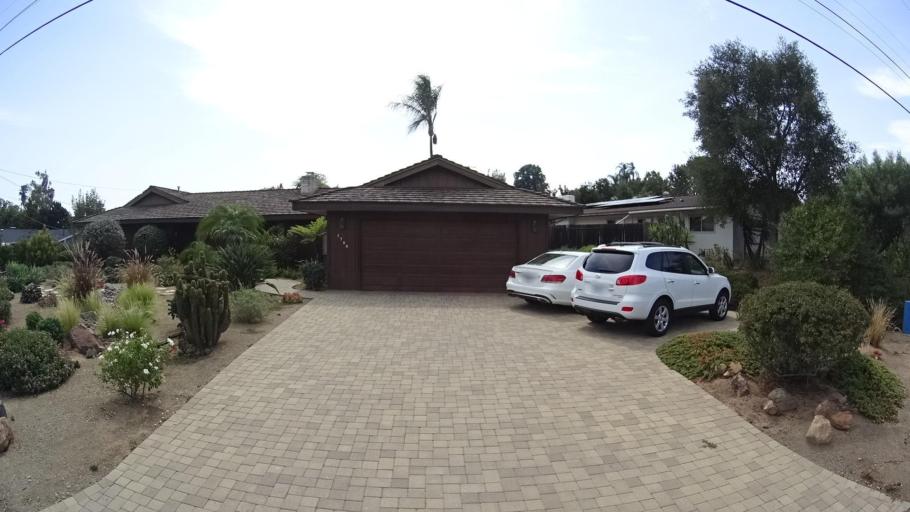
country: US
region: California
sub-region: San Diego County
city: Escondido
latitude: 33.1100
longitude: -117.0403
